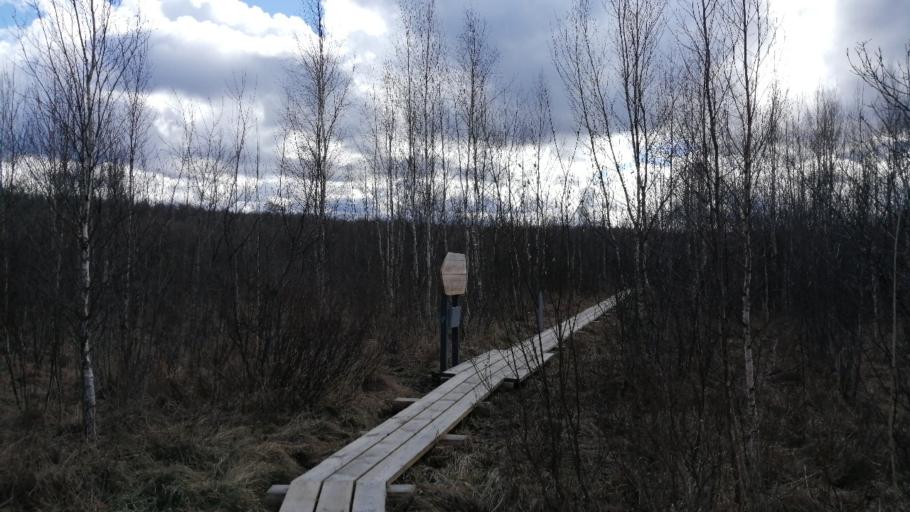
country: EE
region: Tartu
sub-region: Alatskivi vald
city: Kallaste
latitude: 58.3854
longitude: 27.1219
